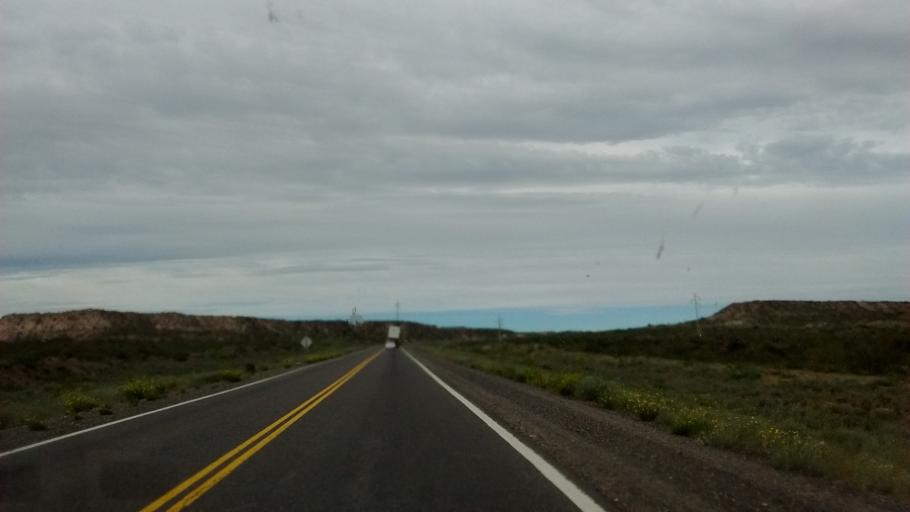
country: AR
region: Rio Negro
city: Catriel
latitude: -38.1983
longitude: -67.9653
